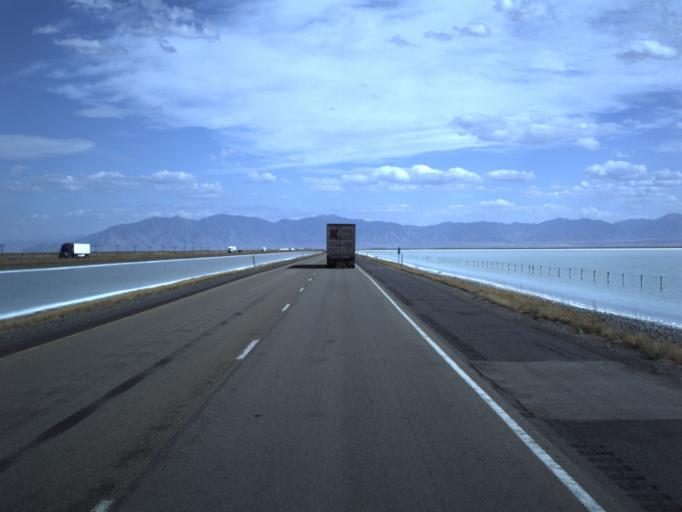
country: US
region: Utah
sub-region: Tooele County
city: Grantsville
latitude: 40.7353
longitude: -112.6077
